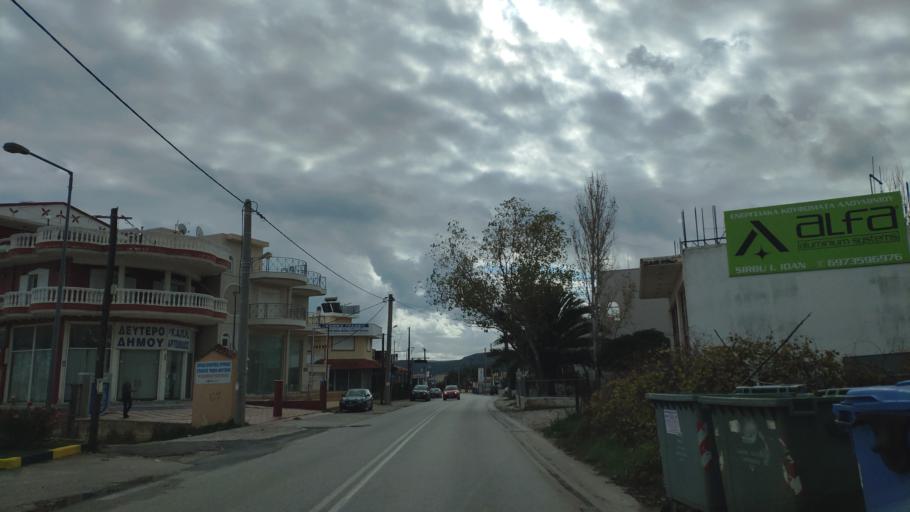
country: GR
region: Attica
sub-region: Nomarchia Anatolikis Attikis
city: Artemida
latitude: 37.9443
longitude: 24.0079
